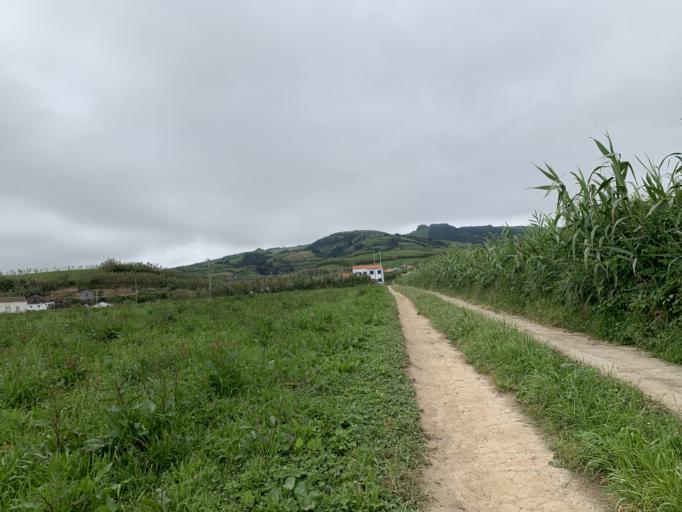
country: PT
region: Azores
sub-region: Ponta Delgada
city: Arrifes
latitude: 37.8519
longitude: -25.8461
